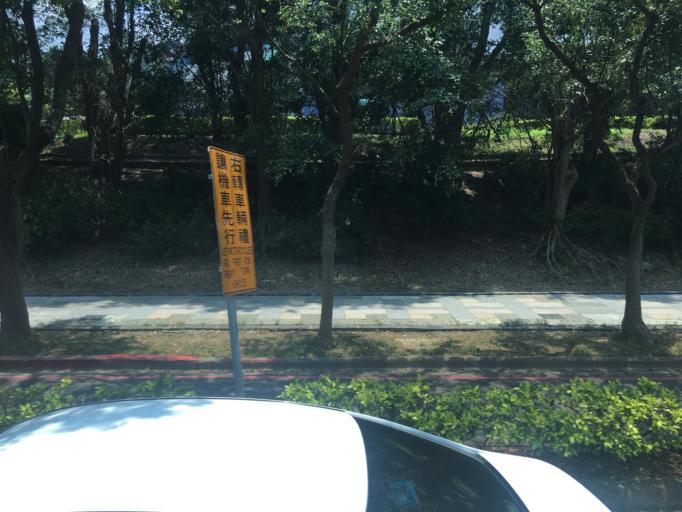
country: TW
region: Taiwan
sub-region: Hsinchu
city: Hsinchu
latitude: 24.7759
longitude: 121.0125
